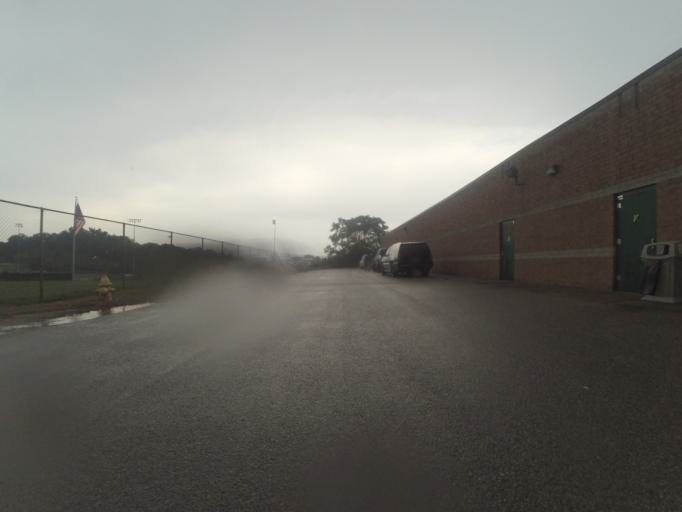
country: US
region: West Virginia
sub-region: Cabell County
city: Huntington
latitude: 38.3950
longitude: -82.3965
